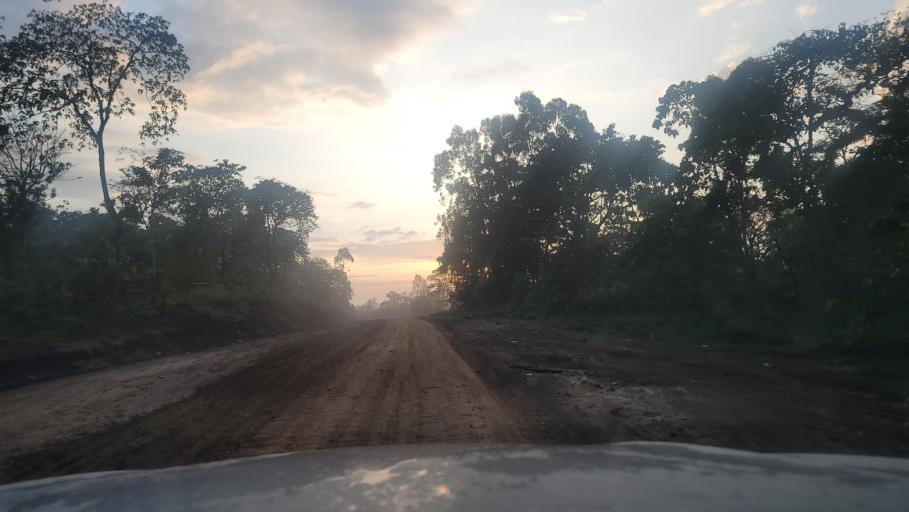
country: ET
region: Oromiya
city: Agaro
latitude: 7.7958
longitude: 36.3787
